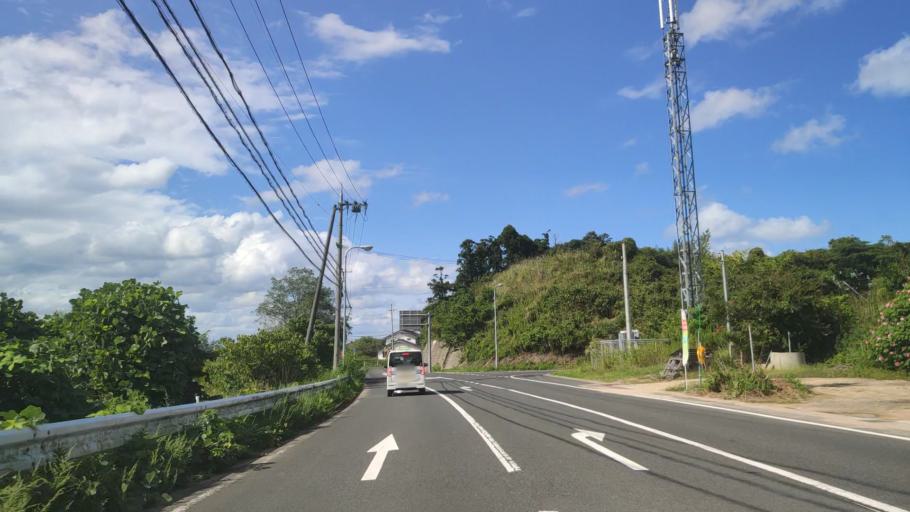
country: JP
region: Hyogo
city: Toyooka
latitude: 35.6418
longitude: 134.9453
